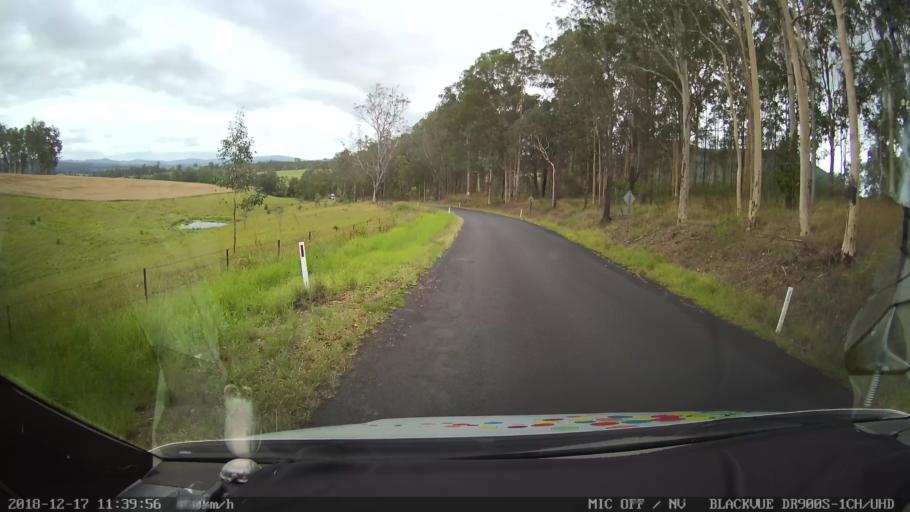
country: AU
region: New South Wales
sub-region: Kyogle
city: Kyogle
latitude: -28.6864
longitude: 152.5922
